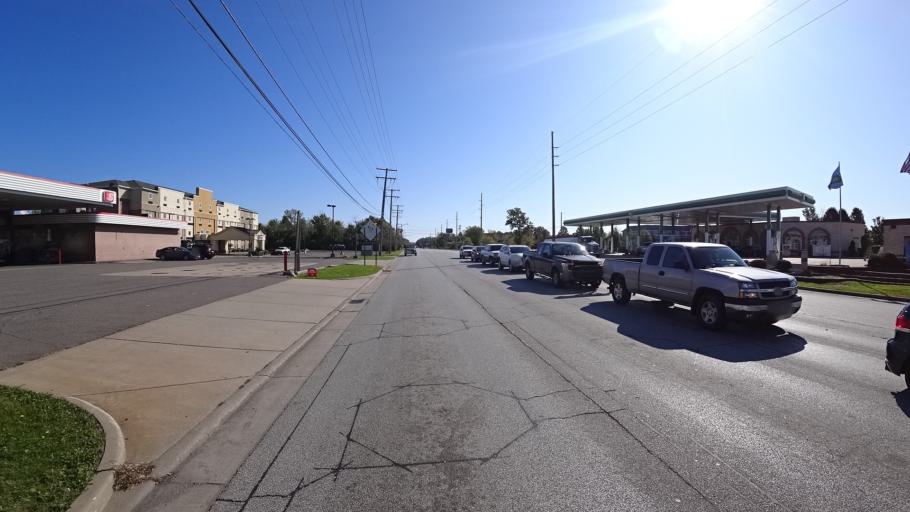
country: US
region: Indiana
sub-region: LaPorte County
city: Michigan City
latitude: 41.6660
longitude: -86.8938
